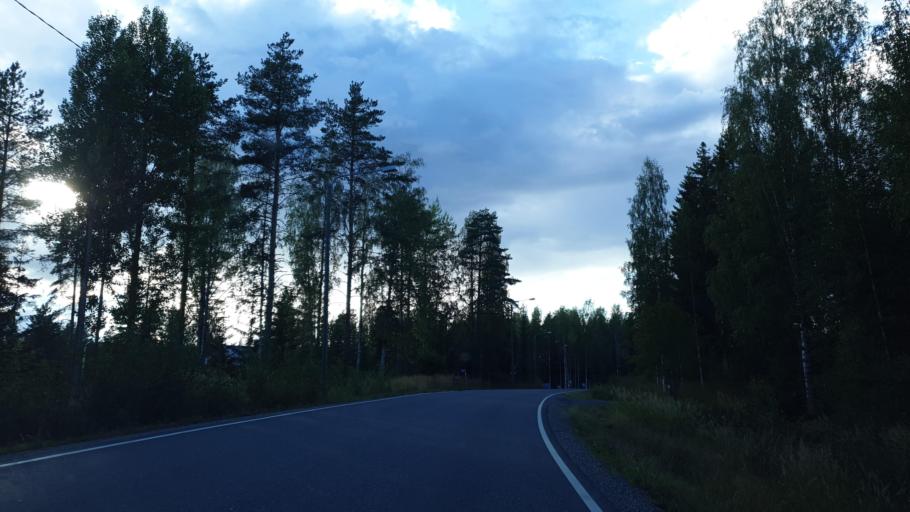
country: FI
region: Northern Savo
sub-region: Koillis-Savo
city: Juankoski
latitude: 63.2032
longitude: 28.2819
